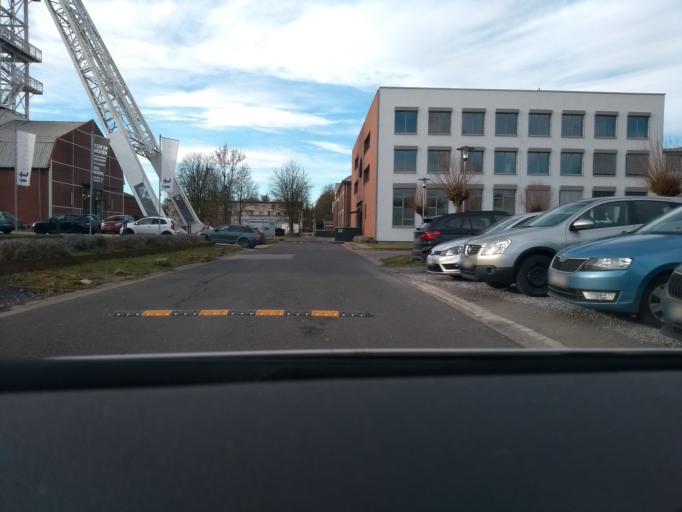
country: DE
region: North Rhine-Westphalia
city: Waltrop
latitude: 51.6053
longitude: 7.4534
